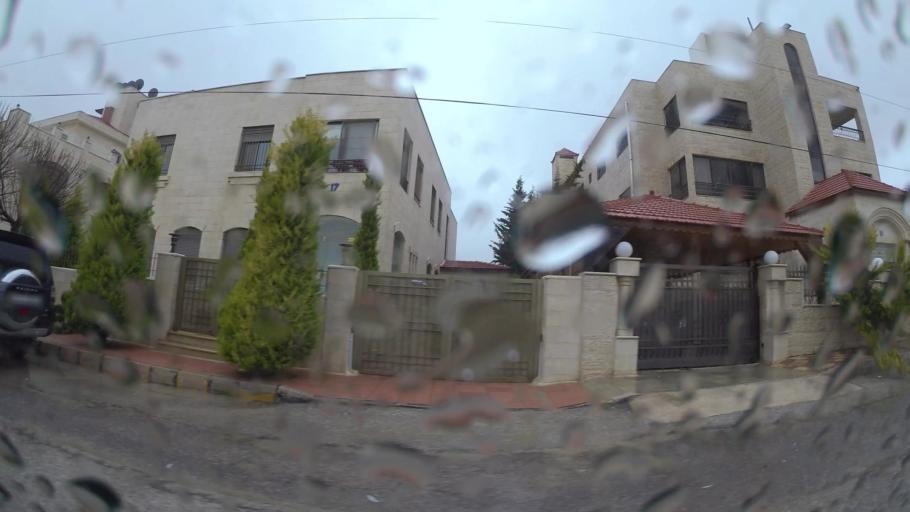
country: JO
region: Amman
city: Al Jubayhah
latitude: 32.0112
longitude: 35.8963
